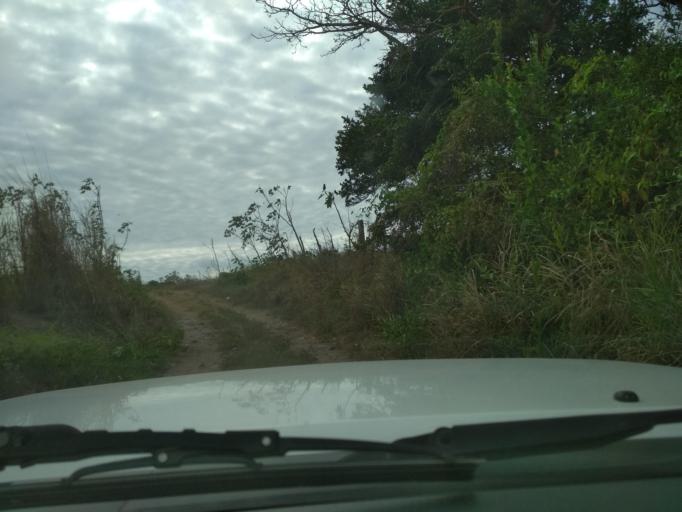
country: MX
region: Veracruz
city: Anton Lizardo
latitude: 19.0484
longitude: -95.9878
